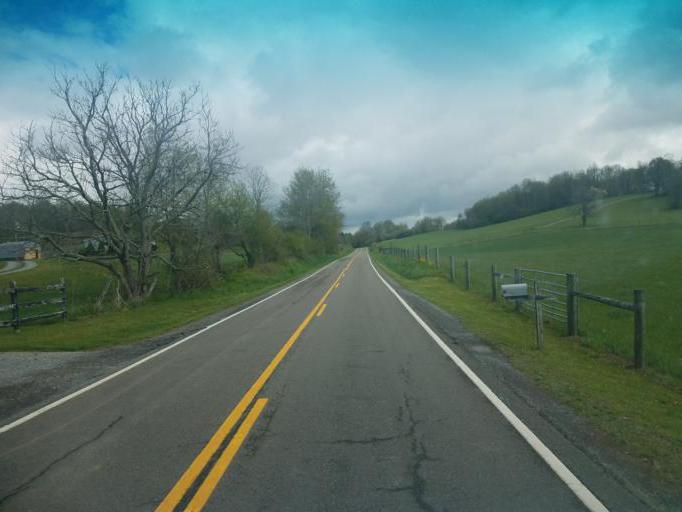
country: US
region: Virginia
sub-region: Wythe County
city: Rural Retreat
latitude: 37.0116
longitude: -81.3573
